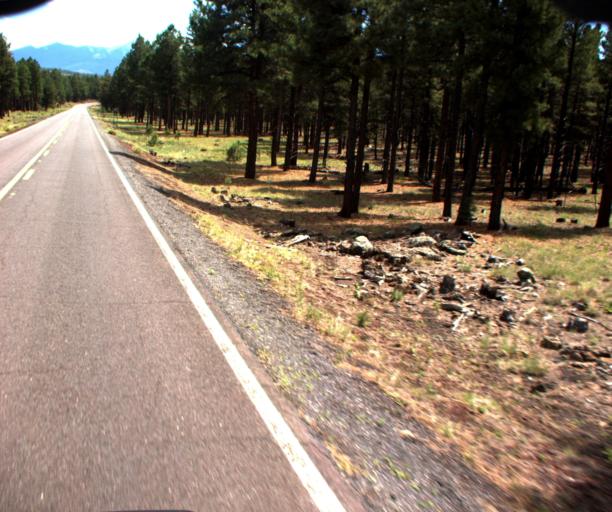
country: US
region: Arizona
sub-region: Coconino County
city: Parks
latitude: 35.4627
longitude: -111.7813
